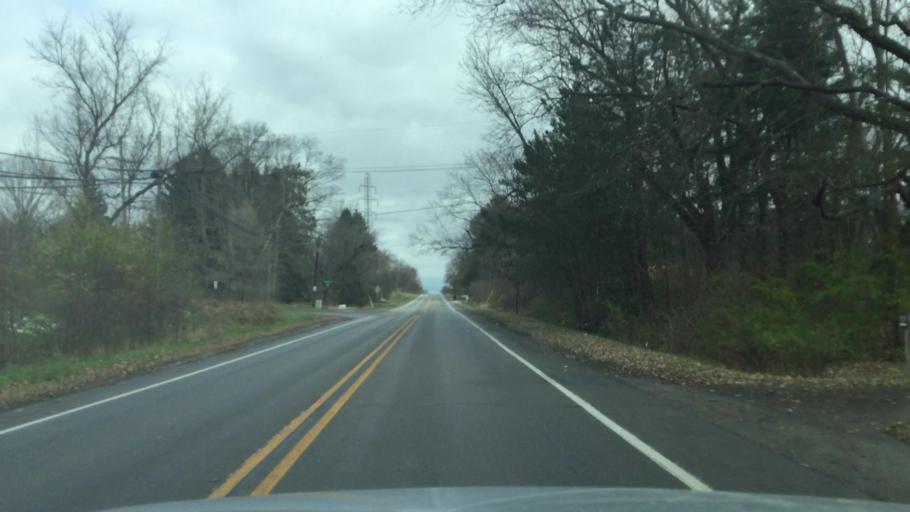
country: US
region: Michigan
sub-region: Washtenaw County
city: Ypsilanti
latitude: 42.3193
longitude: -83.6457
